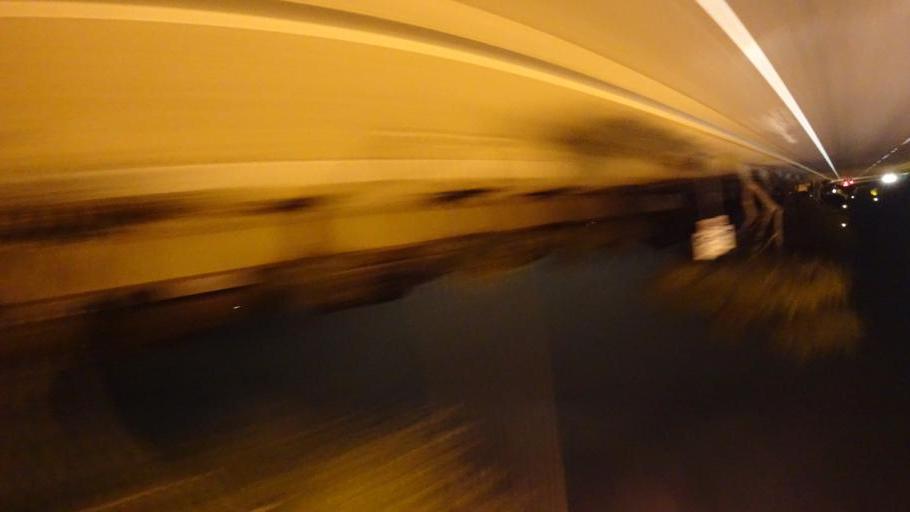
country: US
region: Arizona
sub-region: Maricopa County
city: Queen Creek
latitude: 33.2338
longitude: -111.7066
